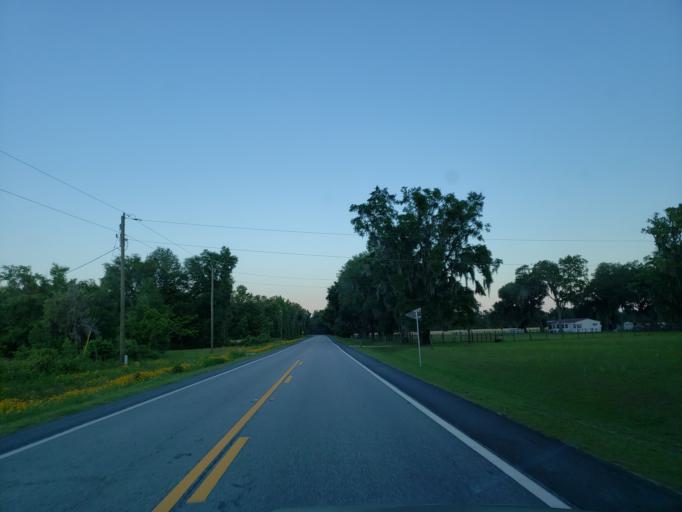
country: US
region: Georgia
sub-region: Echols County
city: Statenville
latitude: 30.5578
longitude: -83.1266
